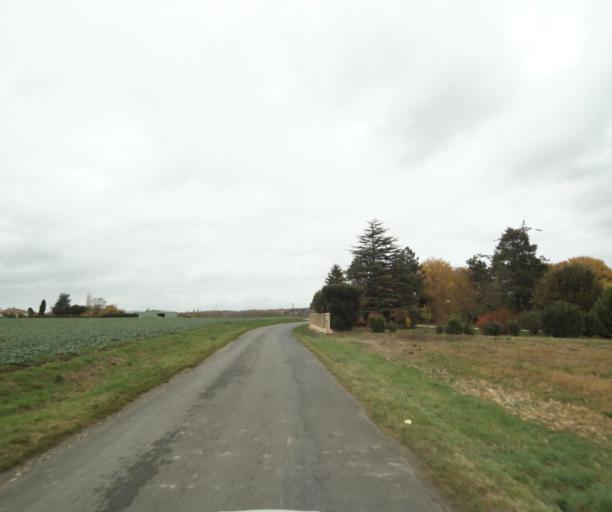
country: FR
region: Poitou-Charentes
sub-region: Departement de la Charente-Maritime
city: Bussac-sur-Charente
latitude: 45.7731
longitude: -0.6432
